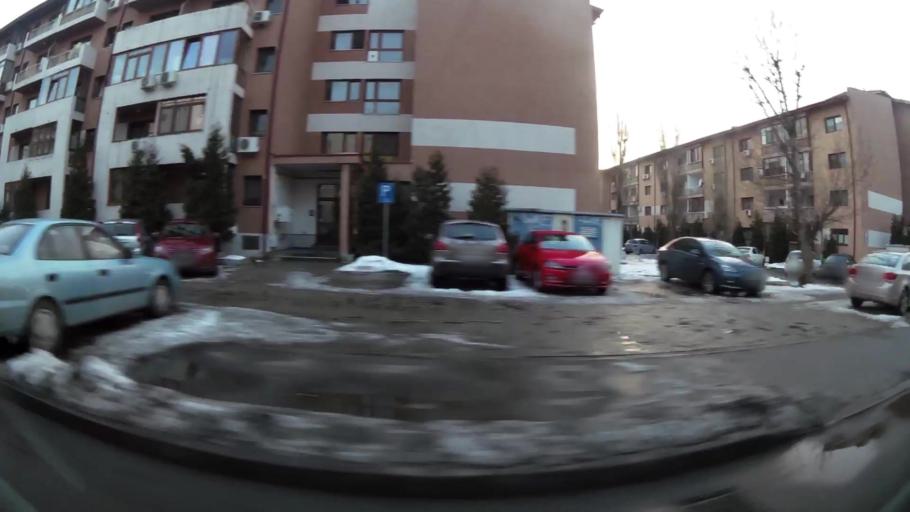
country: RO
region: Ilfov
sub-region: Comuna Fundeni-Dobroesti
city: Fundeni
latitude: 44.4643
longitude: 26.1401
